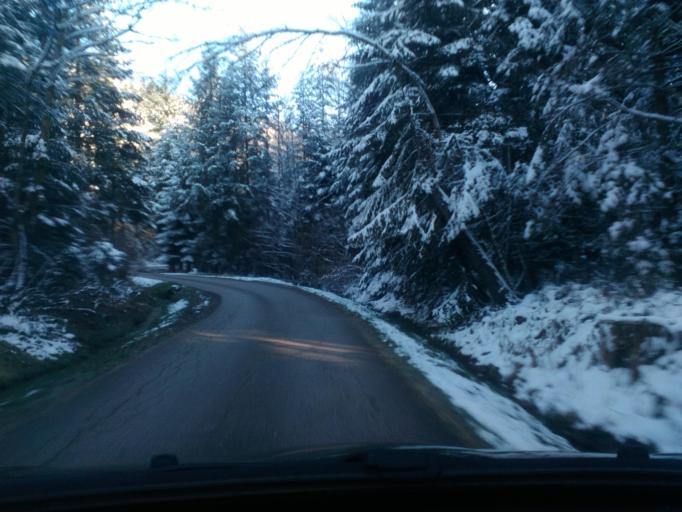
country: FR
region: Lorraine
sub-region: Departement des Vosges
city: Taintrux
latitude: 48.2195
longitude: 6.8719
